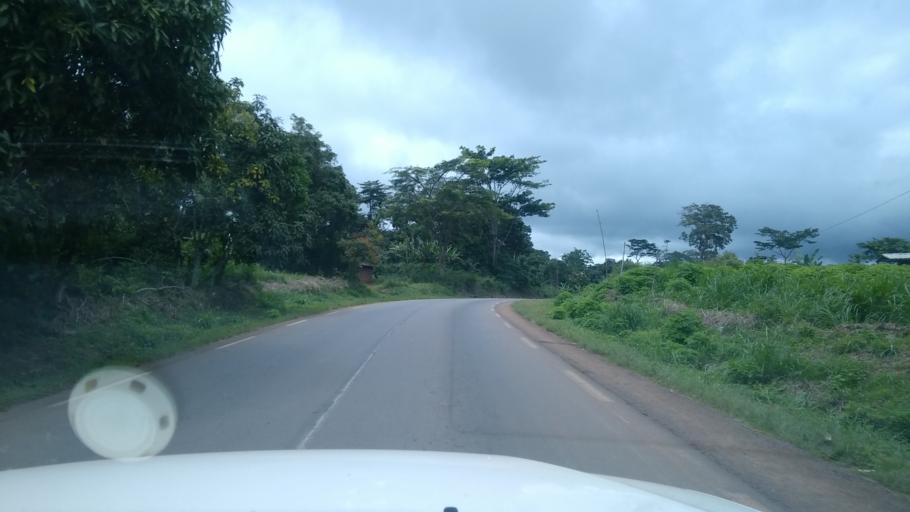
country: CM
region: Centre
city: Mbalmayo
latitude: 3.6004
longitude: 11.5261
